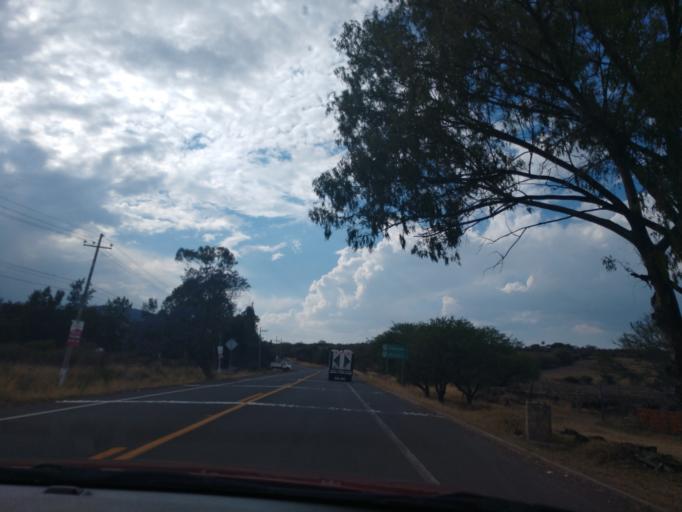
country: MX
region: Jalisco
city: Chapala
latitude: 20.1537
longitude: -103.1875
